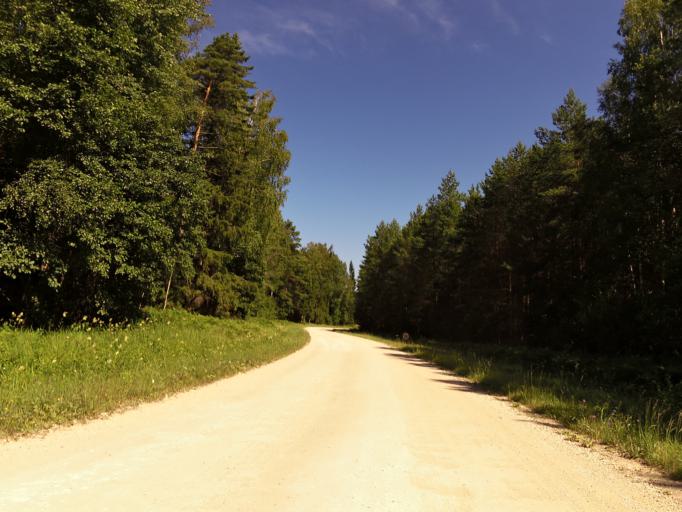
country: EE
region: Hiiumaa
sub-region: Kaerdla linn
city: Kardla
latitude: 58.9223
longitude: 22.3657
